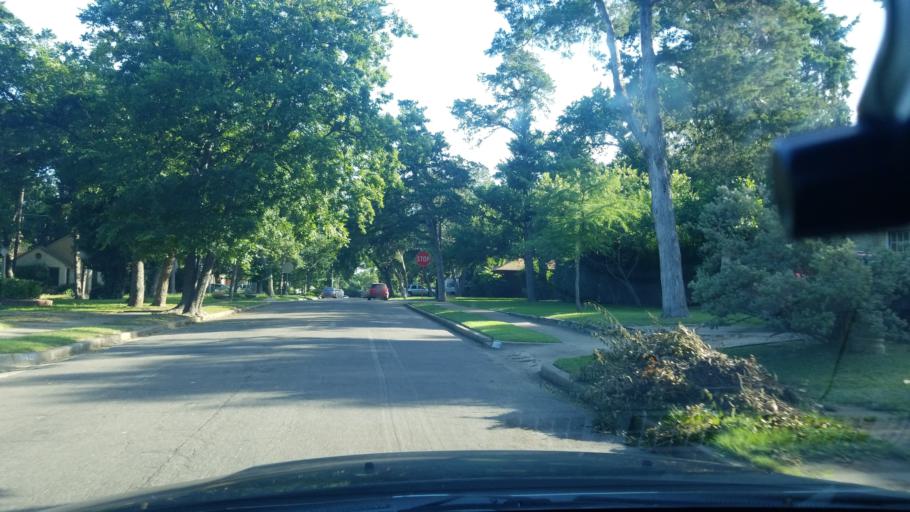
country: US
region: Texas
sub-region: Dallas County
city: Dallas
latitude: 32.7308
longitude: -96.8189
